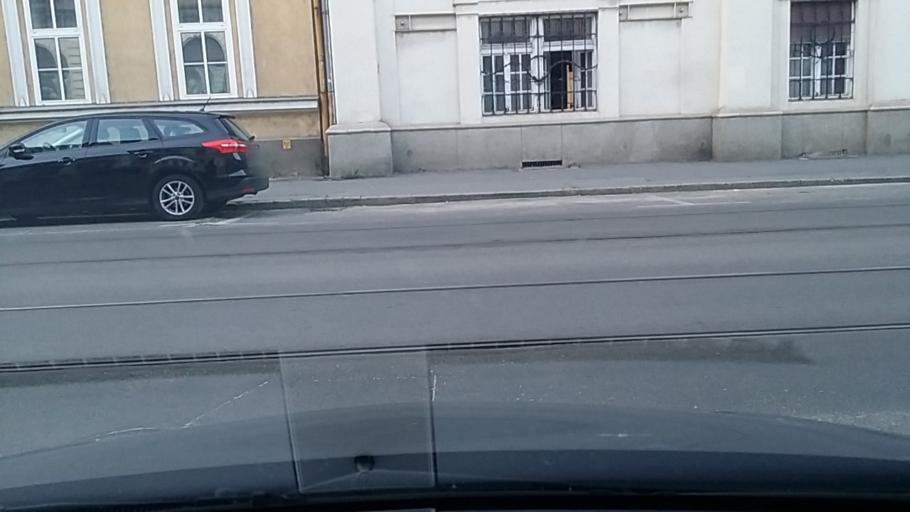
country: HU
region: Borsod-Abauj-Zemplen
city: Miskolc
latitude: 48.1036
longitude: 20.7770
